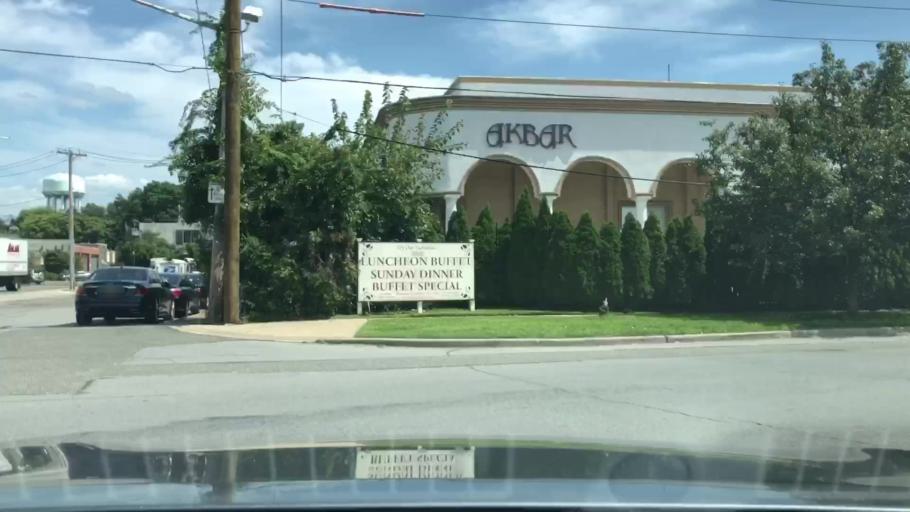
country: US
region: New York
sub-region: Nassau County
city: East Garden City
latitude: 40.7349
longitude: -73.6059
